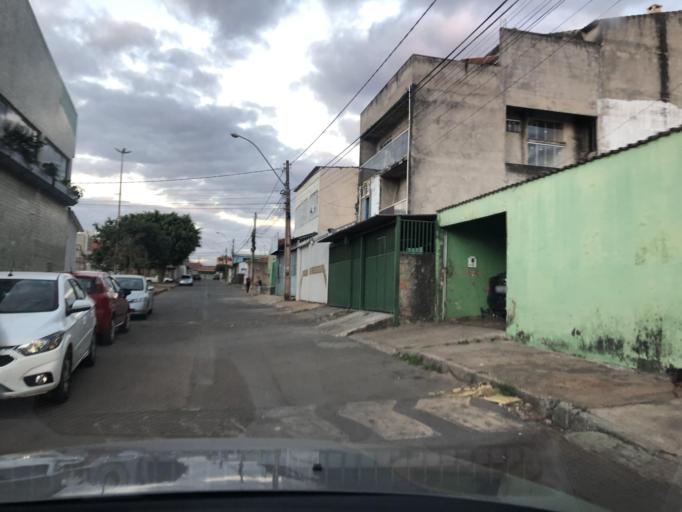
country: BR
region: Federal District
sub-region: Brasilia
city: Brasilia
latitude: -15.8778
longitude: -48.0979
